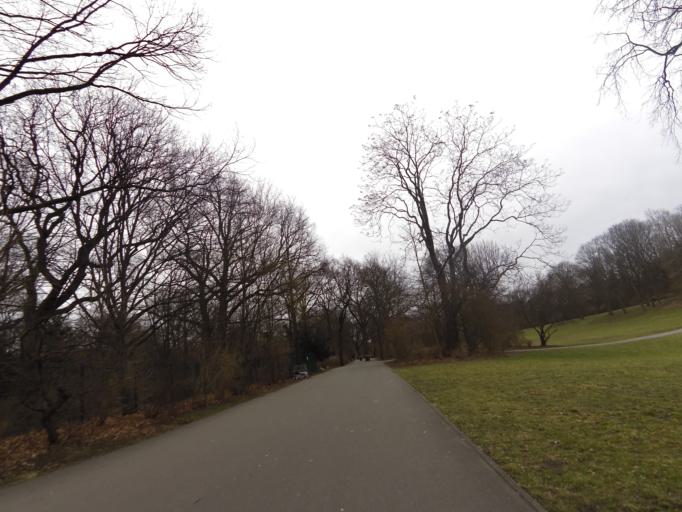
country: DE
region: Berlin
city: Bezirk Kreuzberg
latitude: 52.4849
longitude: 13.4150
